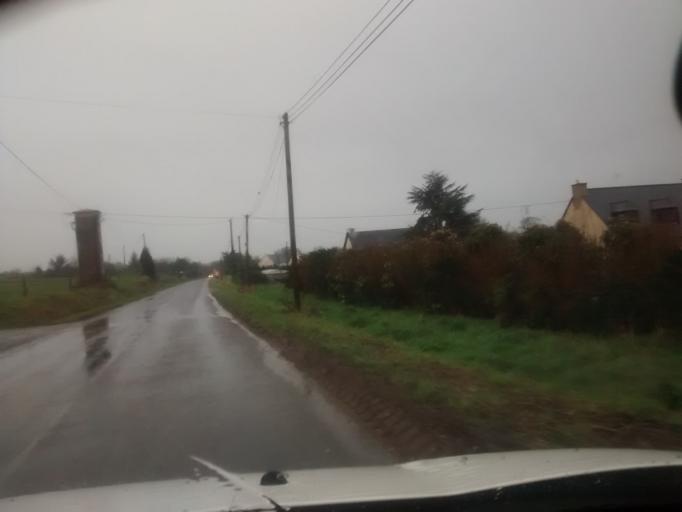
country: FR
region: Brittany
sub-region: Departement d'Ille-et-Vilaine
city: Saint-Pere
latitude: 48.5693
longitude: -1.9090
